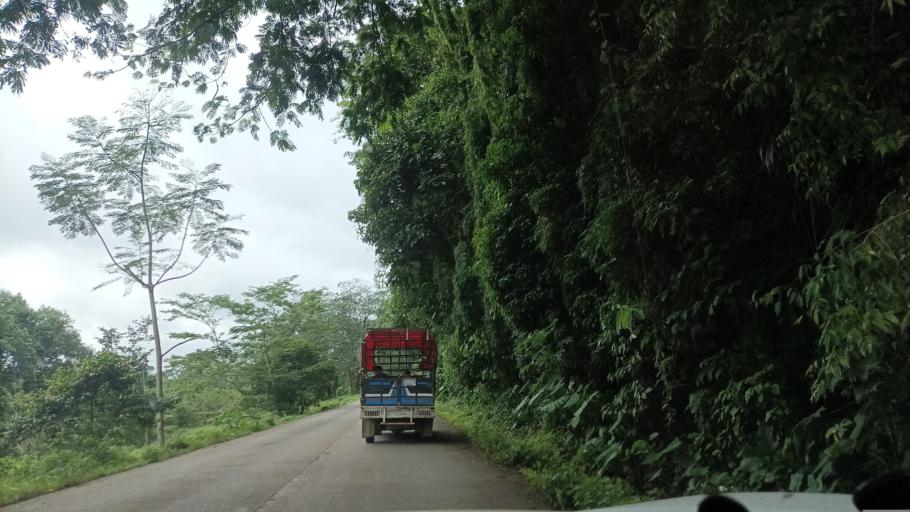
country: MX
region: Veracruz
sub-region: Uxpanapa
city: Poblado 10
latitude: 17.2771
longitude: -94.4916
